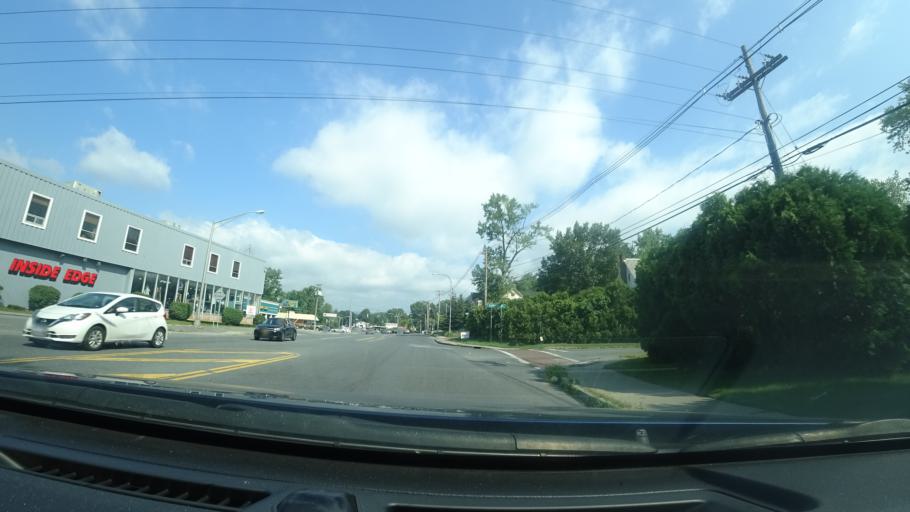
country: US
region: New York
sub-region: Warren County
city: Glens Falls North
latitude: 43.3245
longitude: -73.6626
